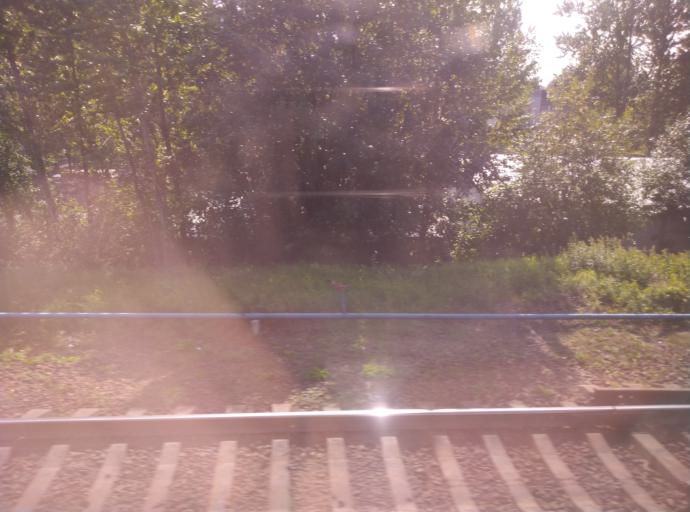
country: RU
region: St.-Petersburg
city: Centralniy
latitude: 59.9103
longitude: 30.3918
